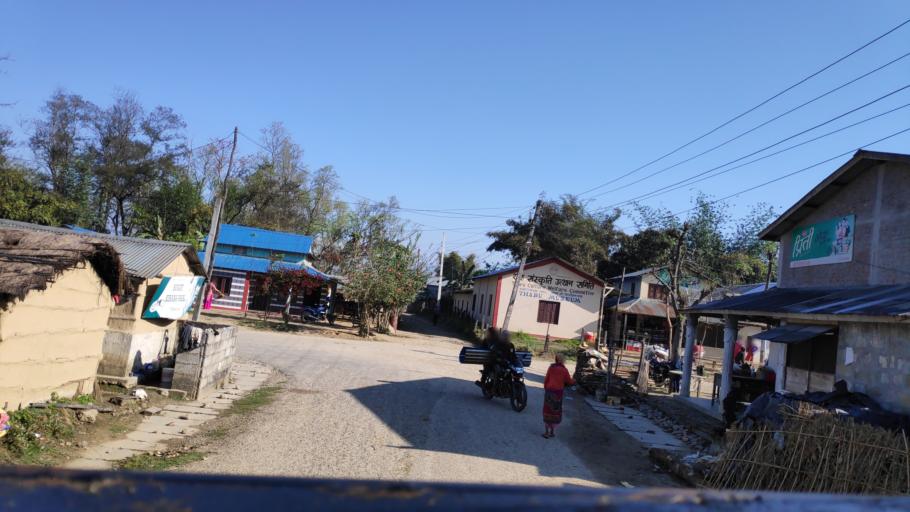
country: NP
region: Central Region
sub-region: Narayani Zone
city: Bharatpur
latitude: 27.5753
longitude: 84.5185
